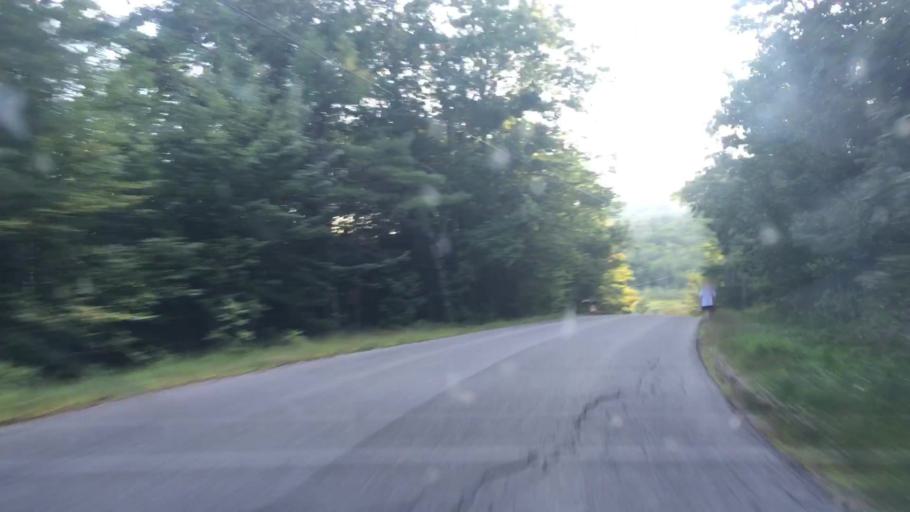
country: US
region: Maine
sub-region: Waldo County
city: Frankfort
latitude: 44.6621
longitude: -68.9285
